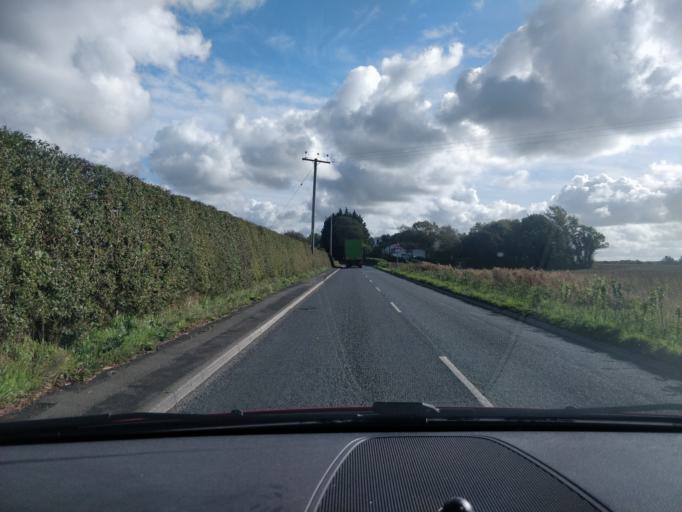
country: GB
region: England
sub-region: Lancashire
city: Ormskirk
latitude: 53.5920
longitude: -2.8895
